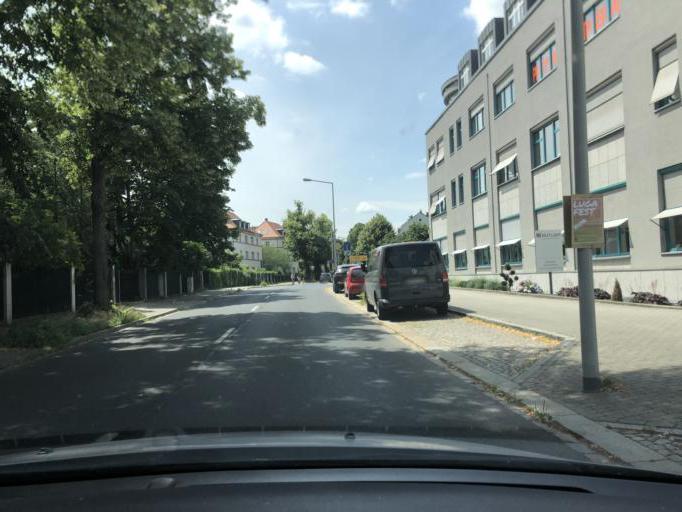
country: DE
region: Saxony
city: Heidenau
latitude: 50.9965
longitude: 13.8213
